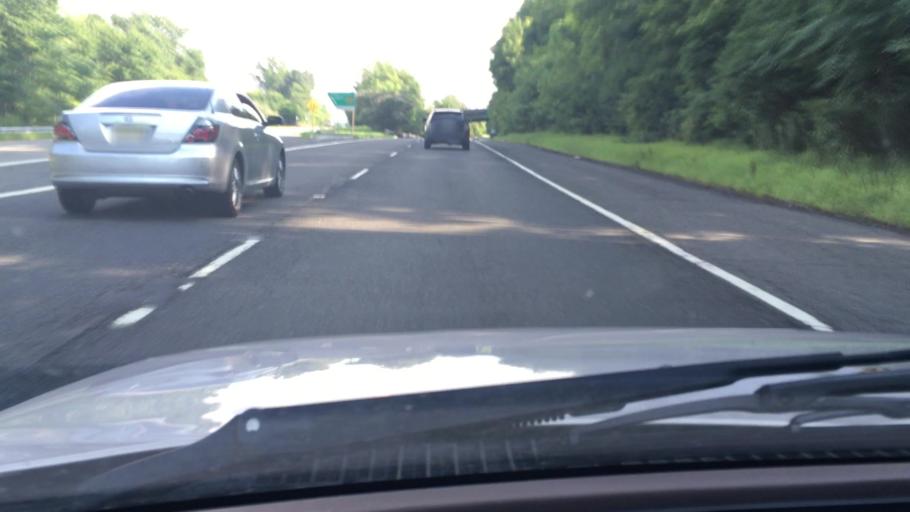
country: US
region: New Jersey
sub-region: Passaic County
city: Clifton
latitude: 40.8844
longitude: -74.1677
